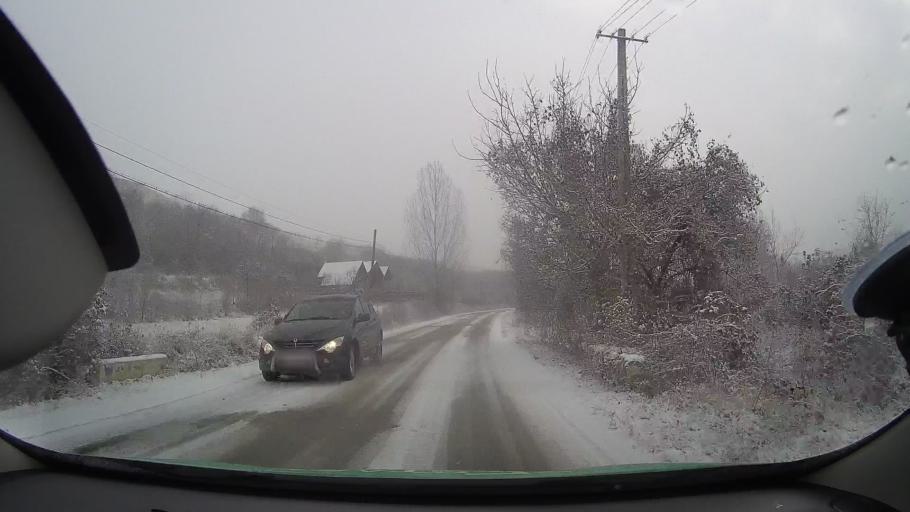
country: RO
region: Alba
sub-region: Municipiul Aiud
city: Aiudul de Sus
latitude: 46.3405
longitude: 23.6667
